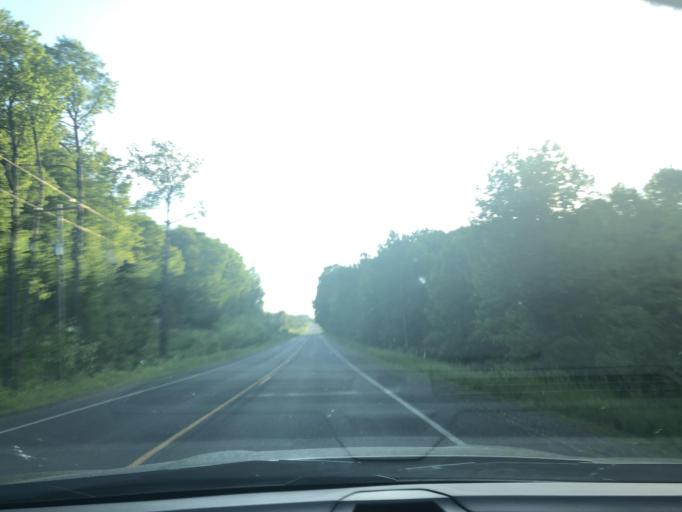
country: US
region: Michigan
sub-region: Missaukee County
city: Lake City
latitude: 44.4665
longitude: -85.0800
